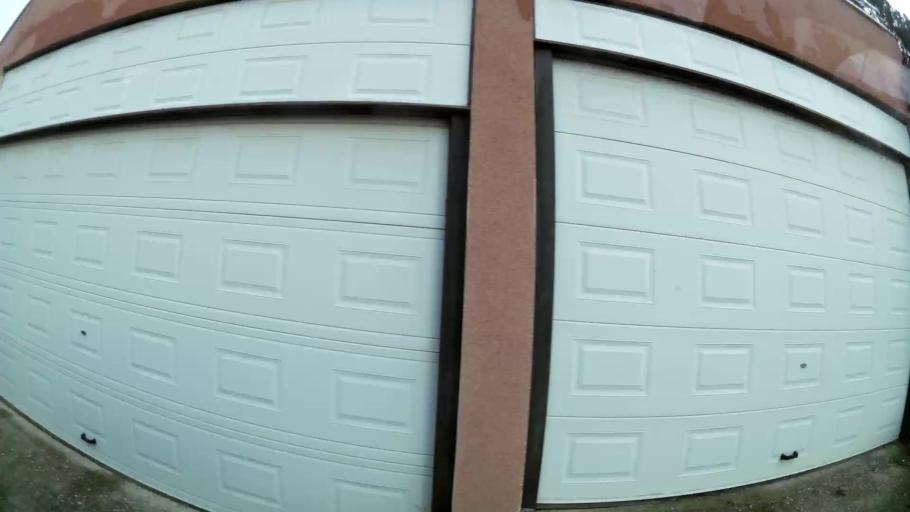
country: XK
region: Pristina
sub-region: Komuna e Prishtines
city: Pristina
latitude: 42.6673
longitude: 21.1821
